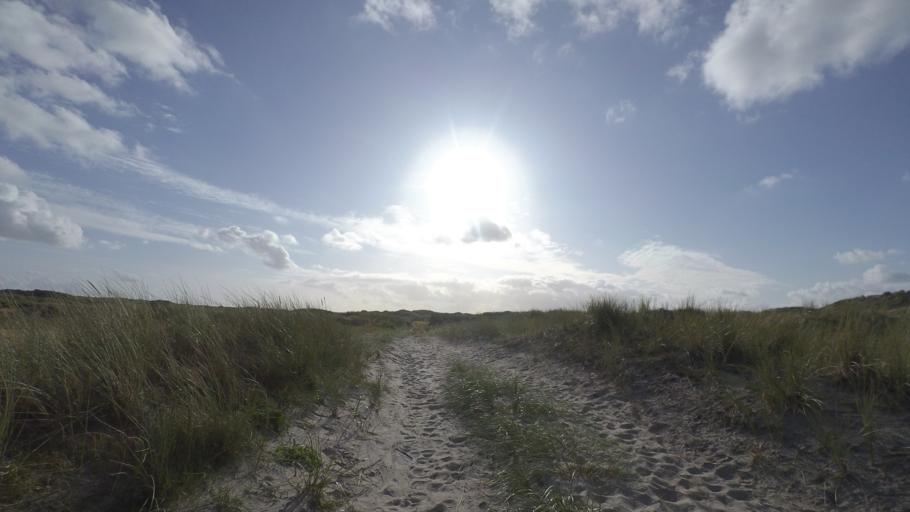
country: NL
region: Friesland
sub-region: Gemeente Dongeradeel
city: Holwerd
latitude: 53.4656
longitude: 5.9064
